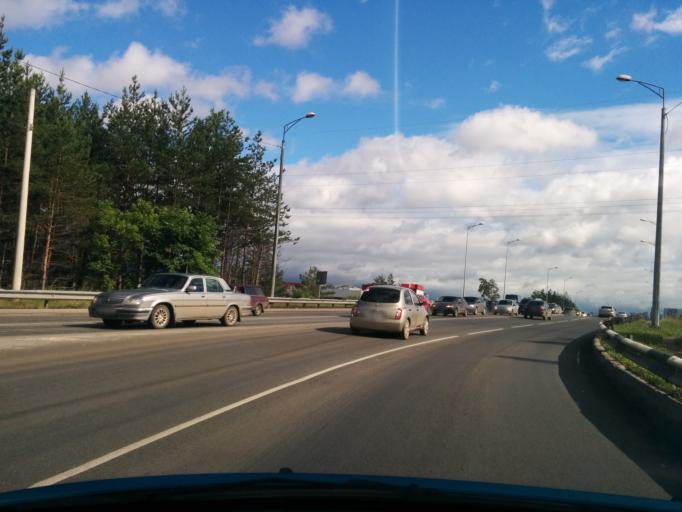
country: RU
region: Perm
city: Perm
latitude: 58.0416
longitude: 56.1869
